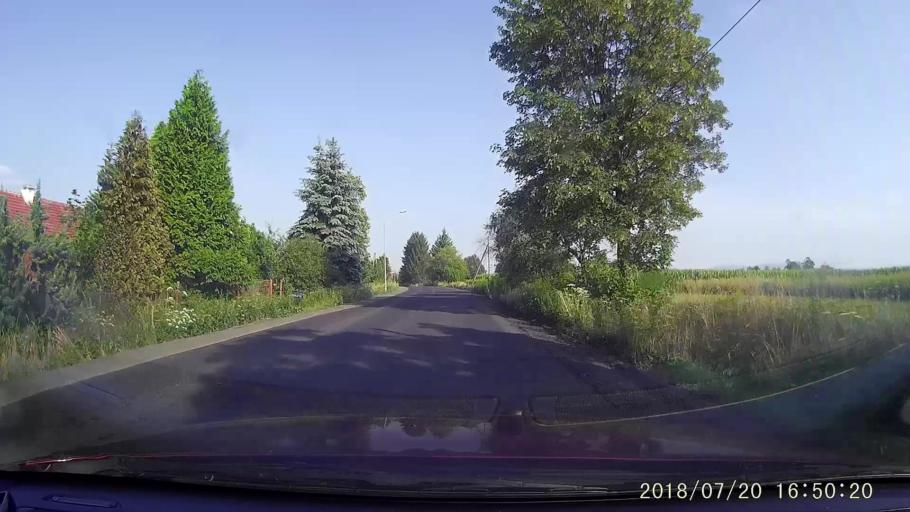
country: PL
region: Lower Silesian Voivodeship
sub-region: Powiat lubanski
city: Lesna
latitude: 51.0431
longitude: 15.2065
